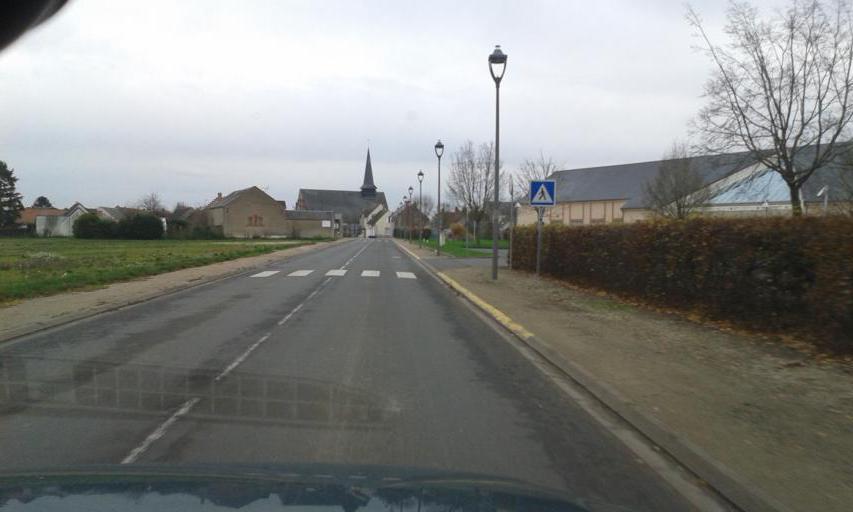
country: FR
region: Centre
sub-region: Departement du Loiret
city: Gidy
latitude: 47.9924
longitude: 1.8370
